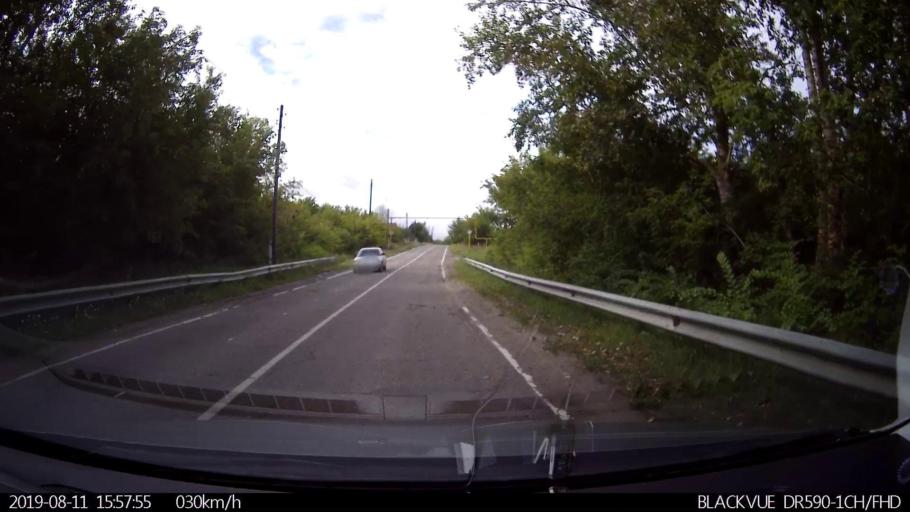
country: RU
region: Ulyanovsk
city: Ignatovka
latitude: 53.9532
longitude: 47.6507
